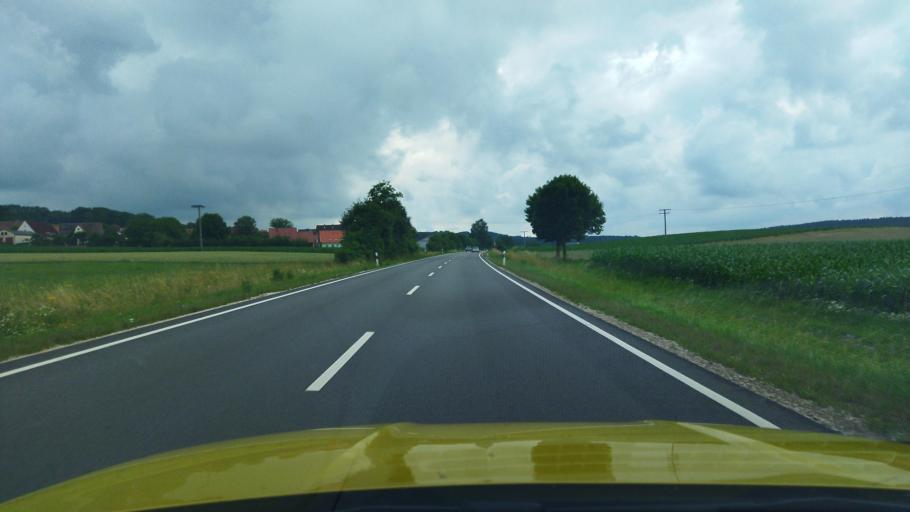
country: DE
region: Bavaria
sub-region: Regierungsbezirk Mittelfranken
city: Absberg
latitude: 49.1099
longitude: 10.8960
